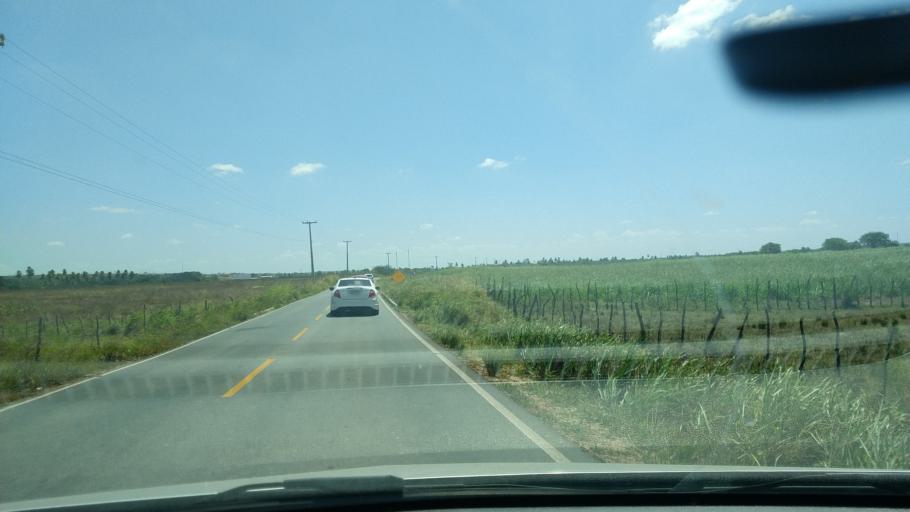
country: BR
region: Rio Grande do Norte
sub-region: Goianinha
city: Goianinha
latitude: -6.2574
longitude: -35.1950
